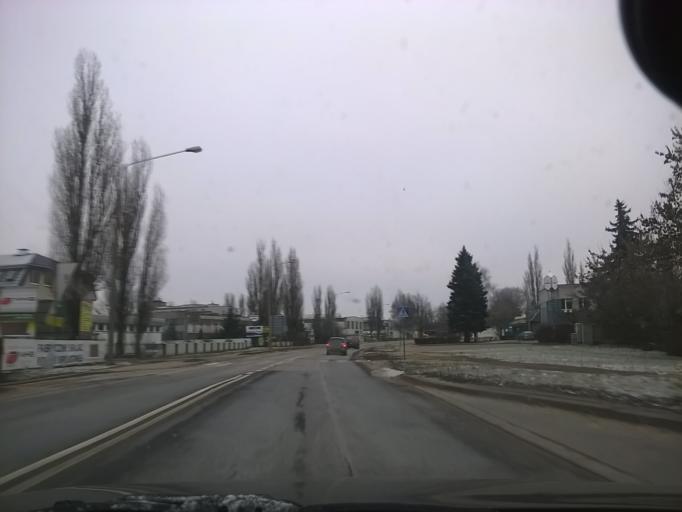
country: PL
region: Warmian-Masurian Voivodeship
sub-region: Powiat olsztynski
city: Olsztyn
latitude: 53.7857
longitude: 20.5354
